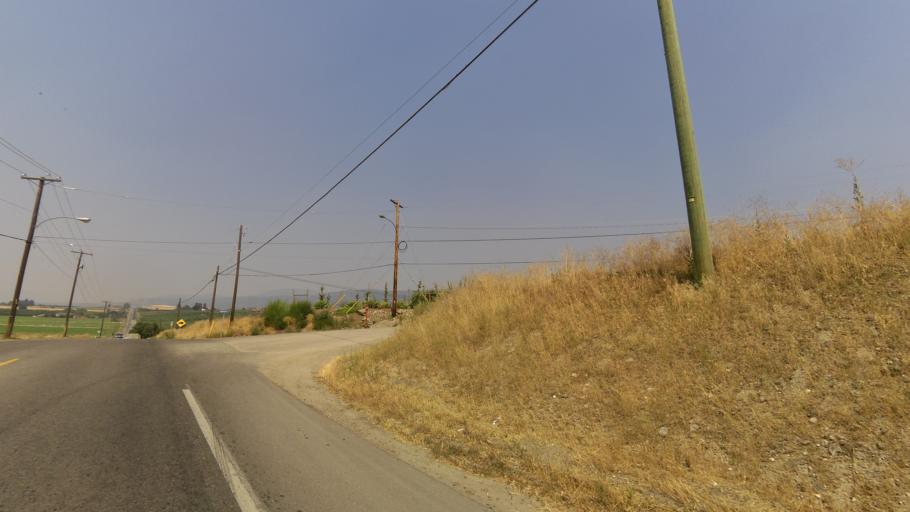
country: CA
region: British Columbia
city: Kelowna
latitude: 49.9197
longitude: -119.3642
